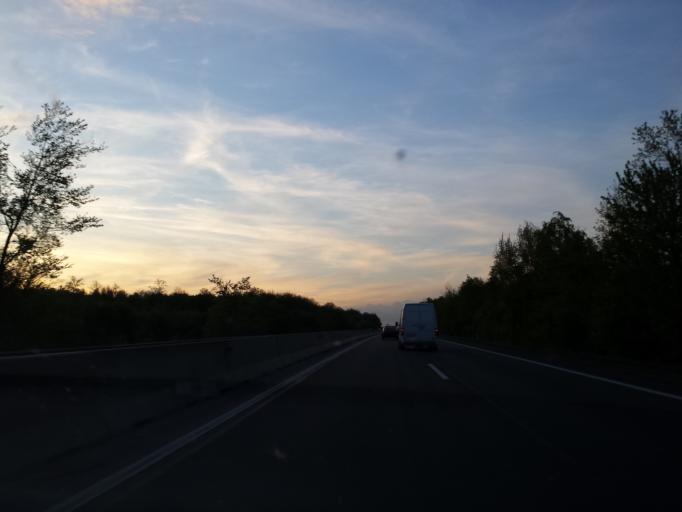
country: AT
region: Lower Austria
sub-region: Politischer Bezirk Ganserndorf
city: Orth an der Donau
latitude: 48.0772
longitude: 16.6799
